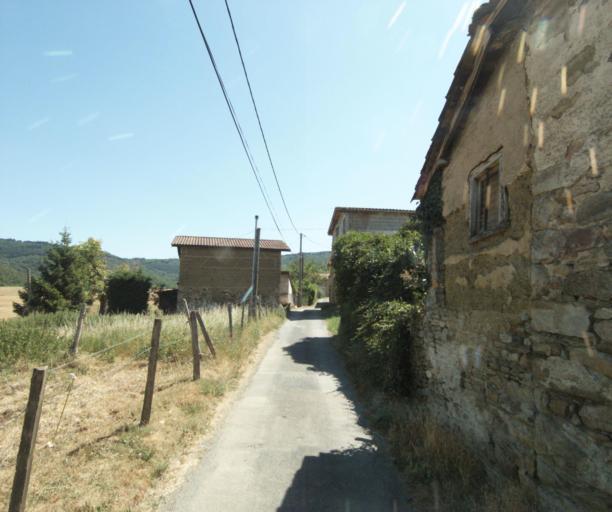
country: FR
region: Rhone-Alpes
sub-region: Departement du Rhone
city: Courzieu
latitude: 45.7598
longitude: 4.5851
